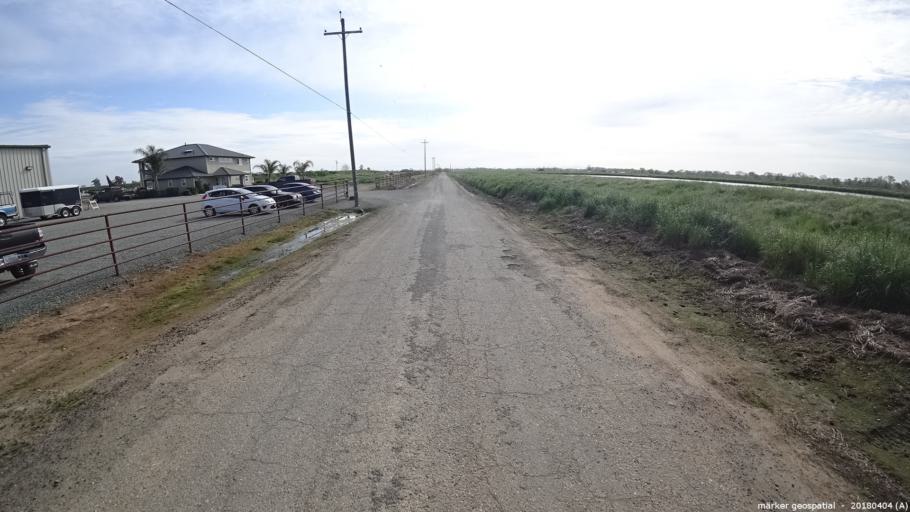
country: US
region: California
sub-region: Sacramento County
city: Herald
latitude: 38.2559
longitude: -121.2205
